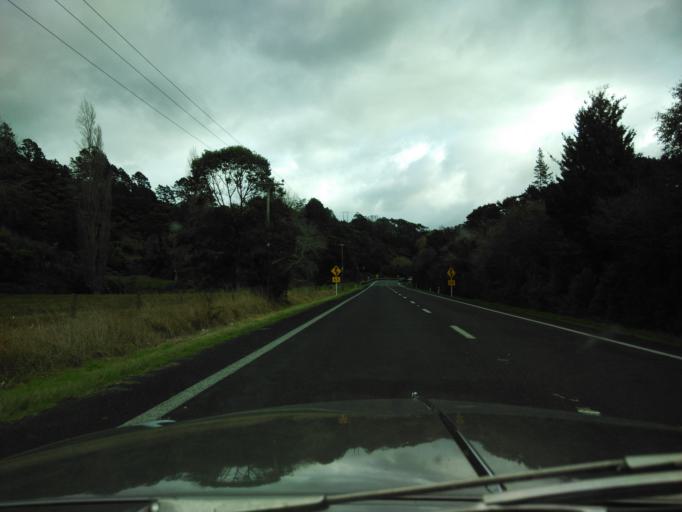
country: NZ
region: Waikato
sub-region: Hauraki District
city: Waihi
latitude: -37.4192
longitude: 175.7500
